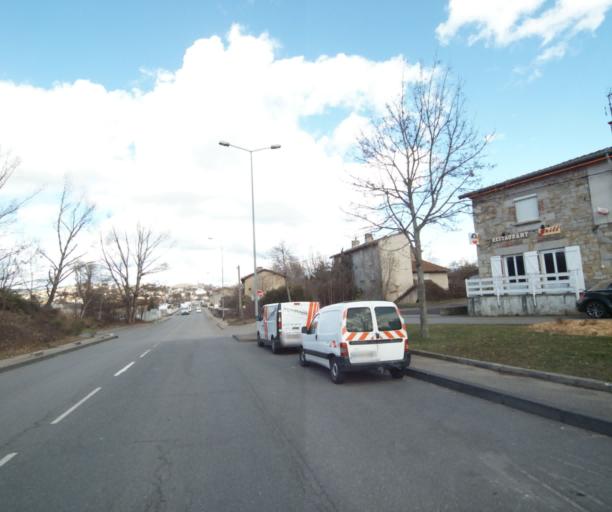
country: FR
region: Rhone-Alpes
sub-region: Departement de la Loire
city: La Talaudiere
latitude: 45.4743
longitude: 4.4421
